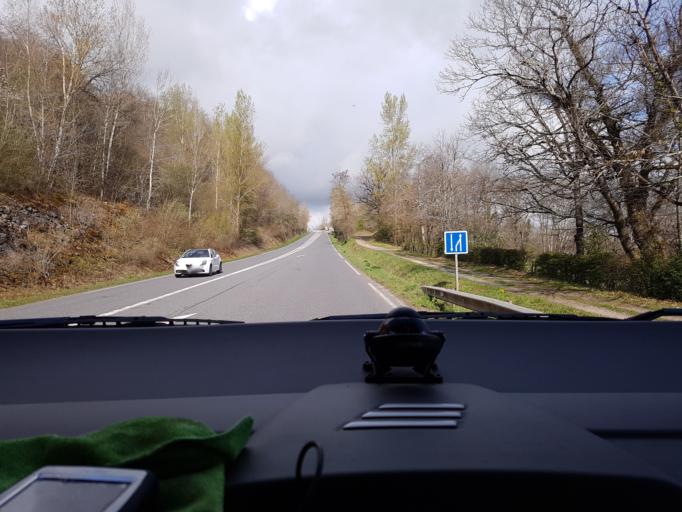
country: FR
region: Midi-Pyrenees
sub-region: Departement de l'Aveyron
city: Moyrazes
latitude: 44.3788
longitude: 2.4342
